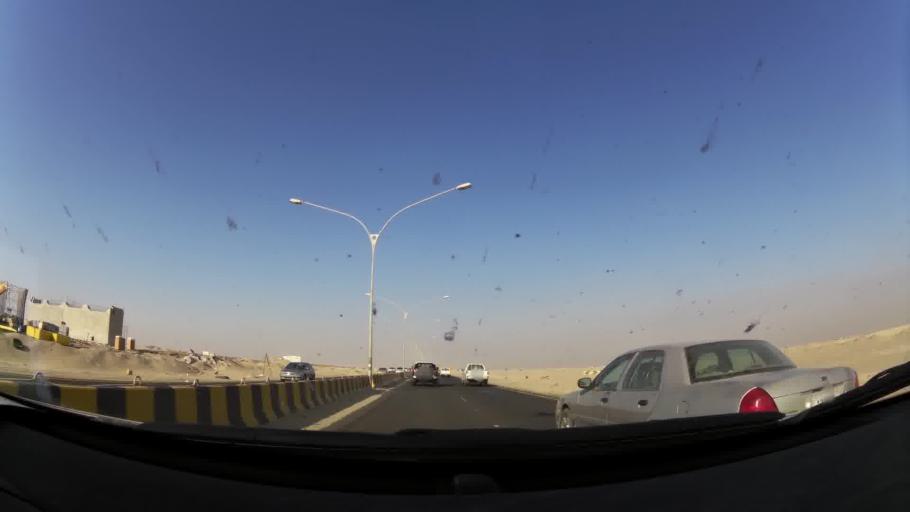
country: KW
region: Al Ahmadi
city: Al Wafrah
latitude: 28.8164
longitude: 48.0471
